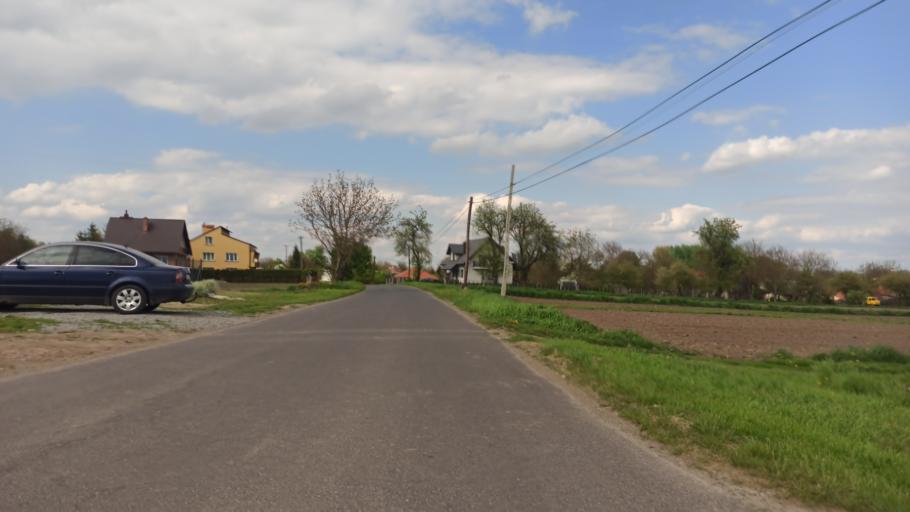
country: PL
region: Subcarpathian Voivodeship
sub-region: Powiat jaroslawski
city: Radymno
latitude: 49.9408
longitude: 22.8126
